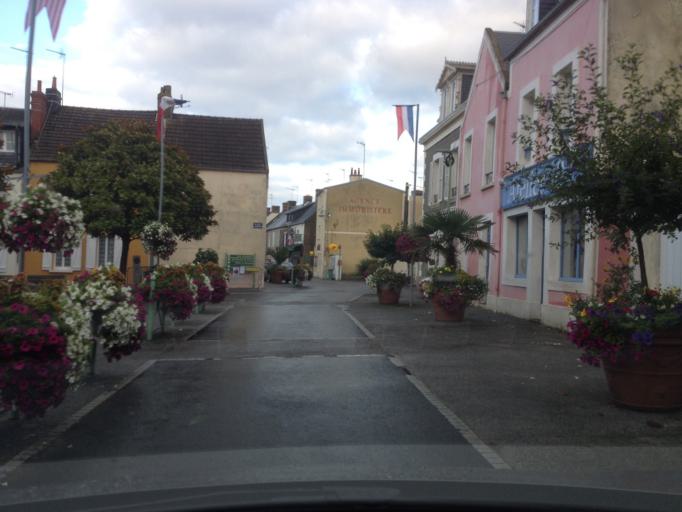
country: FR
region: Lower Normandy
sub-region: Departement du Calvados
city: Grandcamp-Maisy
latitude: 49.3879
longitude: -1.0455
